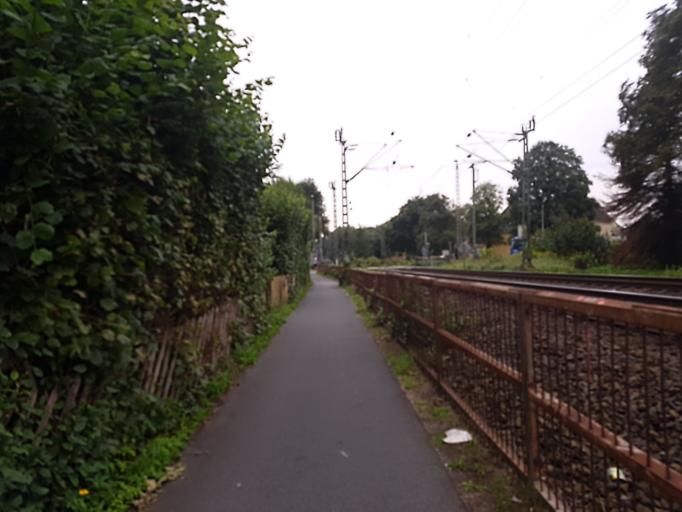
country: DE
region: Lower Saxony
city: Oldenburg
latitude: 53.1384
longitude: 8.2367
